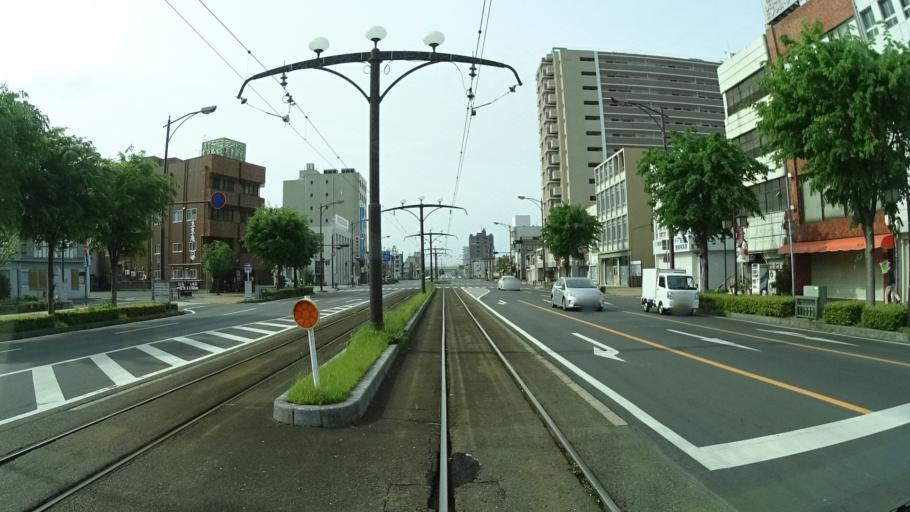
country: JP
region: Aichi
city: Toyohashi
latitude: 34.7646
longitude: 137.3901
